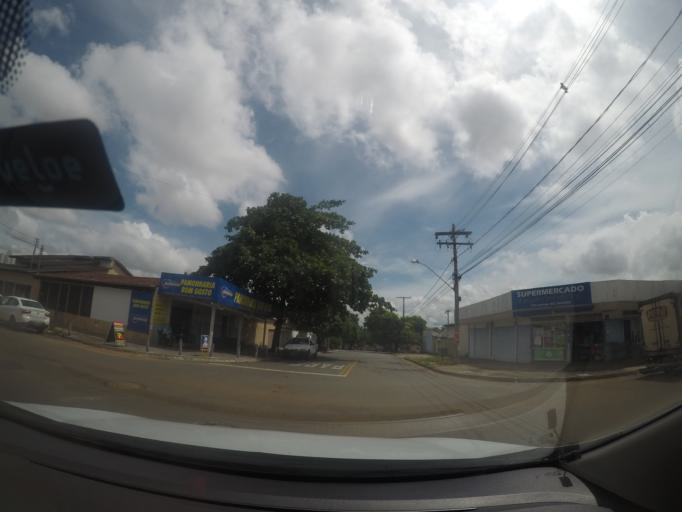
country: BR
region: Goias
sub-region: Goiania
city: Goiania
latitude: -16.7171
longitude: -49.3175
